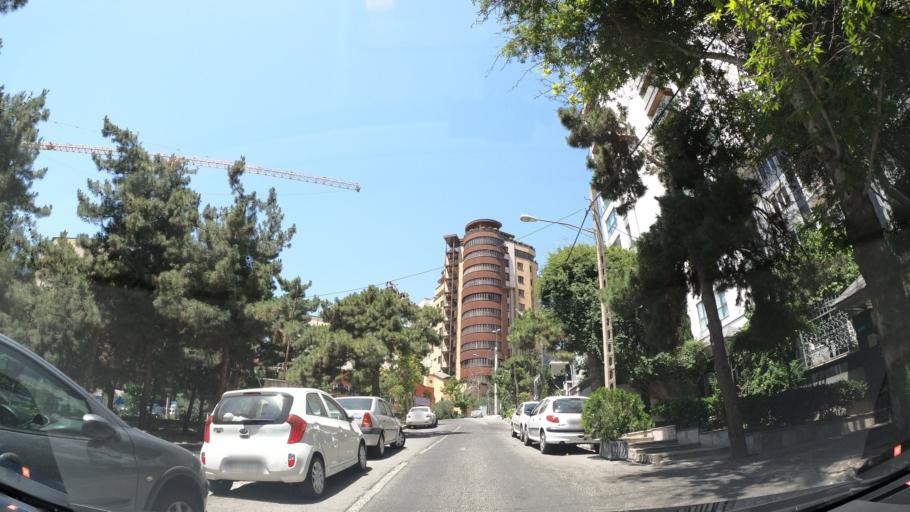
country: IR
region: Tehran
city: Tajrish
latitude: 35.7892
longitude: 51.3819
